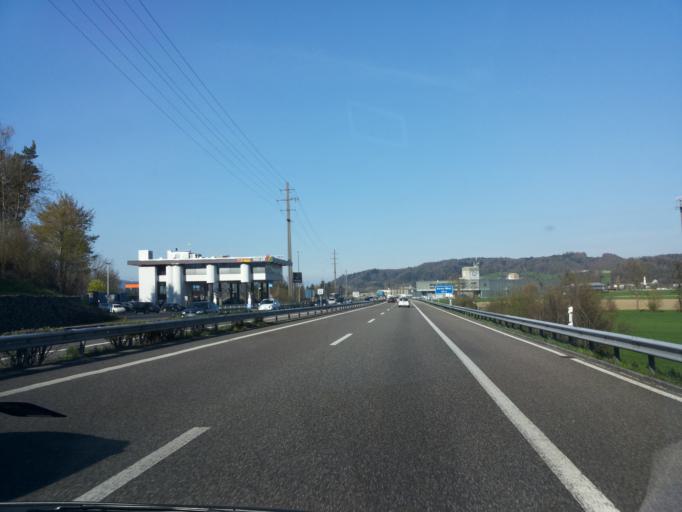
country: CH
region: Aargau
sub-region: Bezirk Zofingen
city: Kolliken
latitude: 47.3288
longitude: 8.0295
